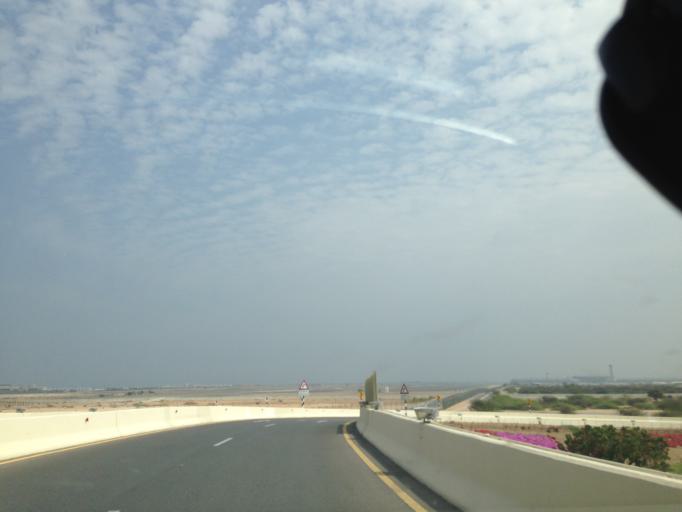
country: OM
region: Muhafazat Masqat
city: As Sib al Jadidah
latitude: 23.6017
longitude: 58.2494
